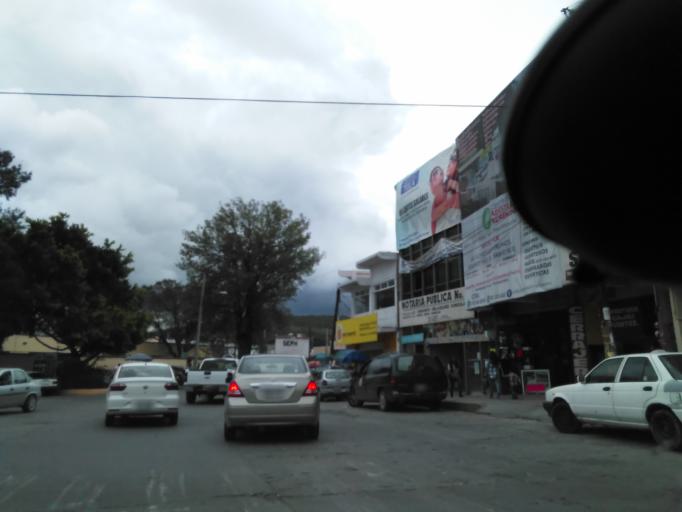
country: MX
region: Hidalgo
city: Tula de Allende
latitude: 20.0549
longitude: -99.3397
